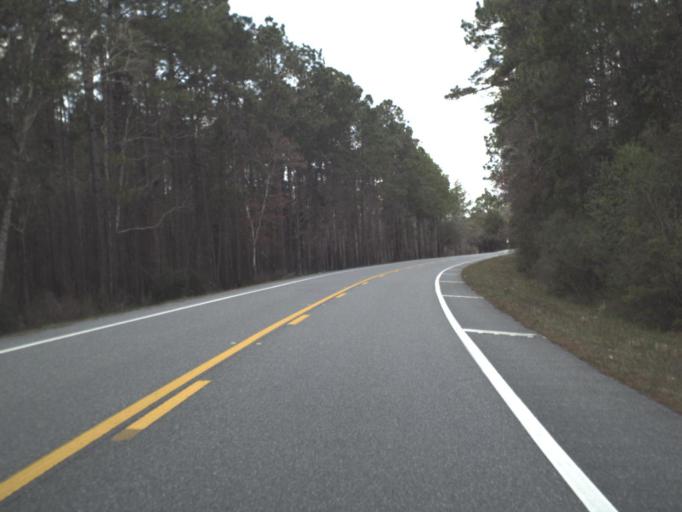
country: US
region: Florida
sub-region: Franklin County
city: Apalachicola
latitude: 29.8503
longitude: -84.9725
